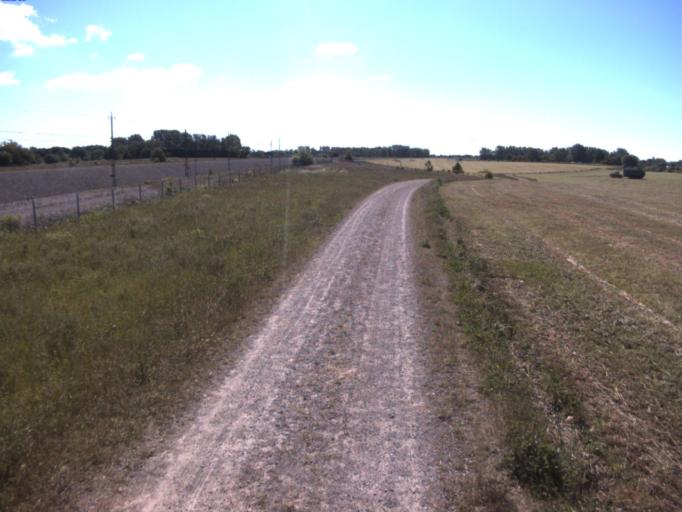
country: SE
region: Skane
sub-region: Helsingborg
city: Rydeback
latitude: 55.9965
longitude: 12.7649
